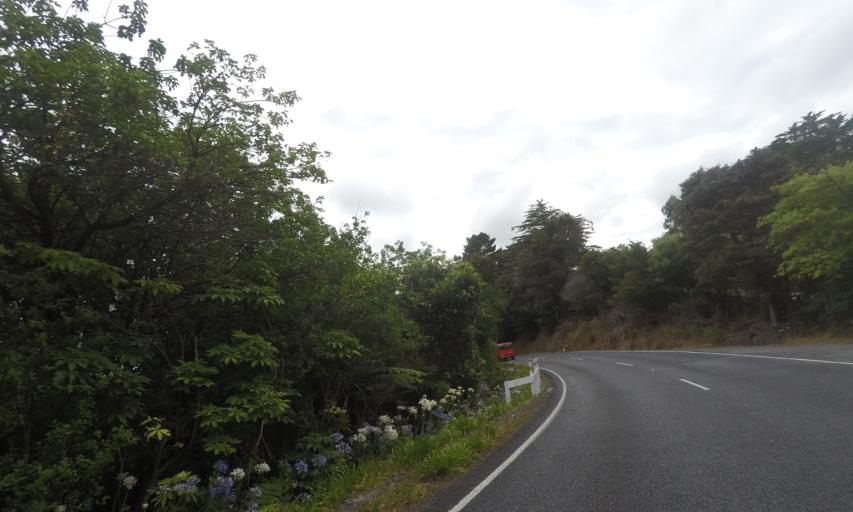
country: NZ
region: Northland
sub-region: Whangarei
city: Whangarei
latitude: -35.7651
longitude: 174.4629
